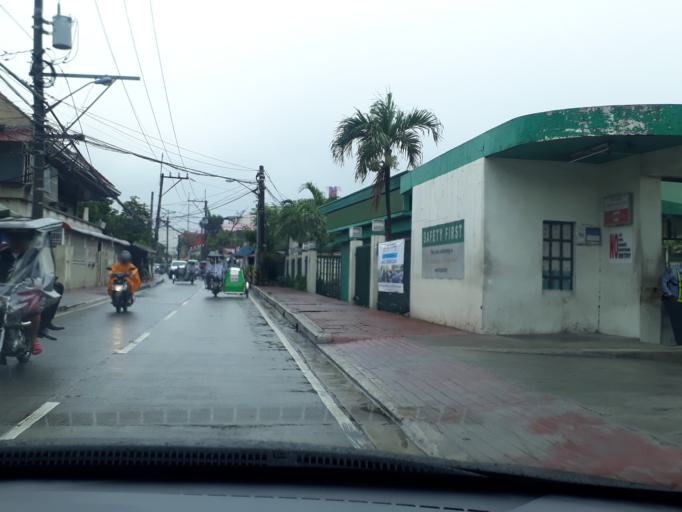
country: PH
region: Calabarzon
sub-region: Province of Rizal
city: Valenzuela
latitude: 14.7128
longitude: 120.9869
